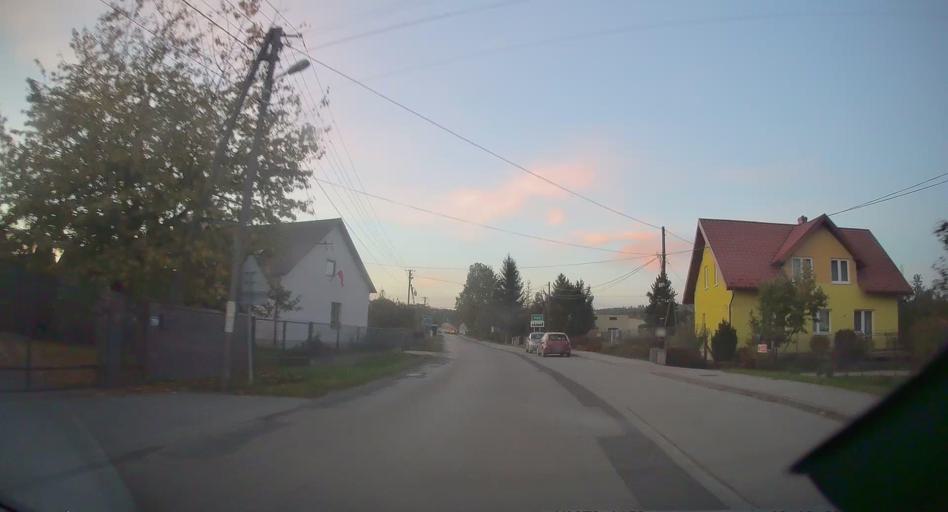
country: PL
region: Lesser Poland Voivodeship
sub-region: Powiat krakowski
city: Zabierzow
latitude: 50.1332
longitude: 19.8214
